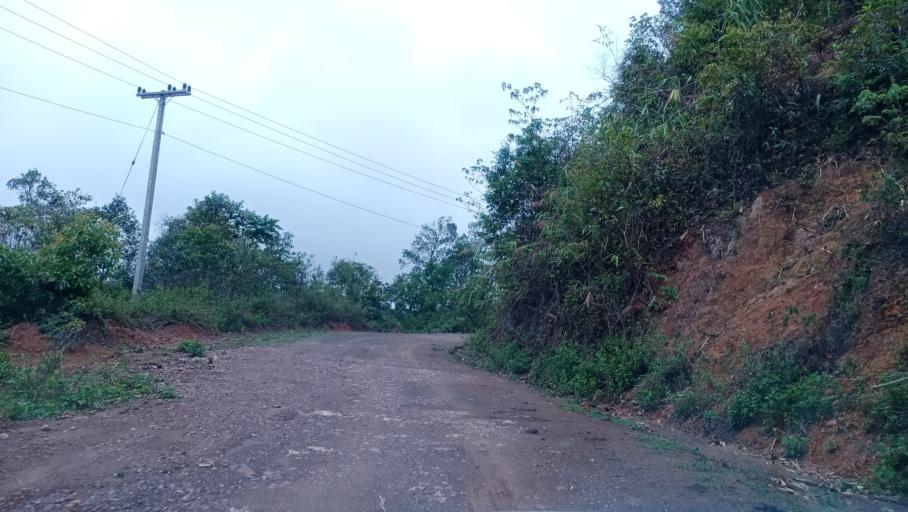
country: LA
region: Phongsali
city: Phongsali
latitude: 21.3488
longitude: 102.0968
